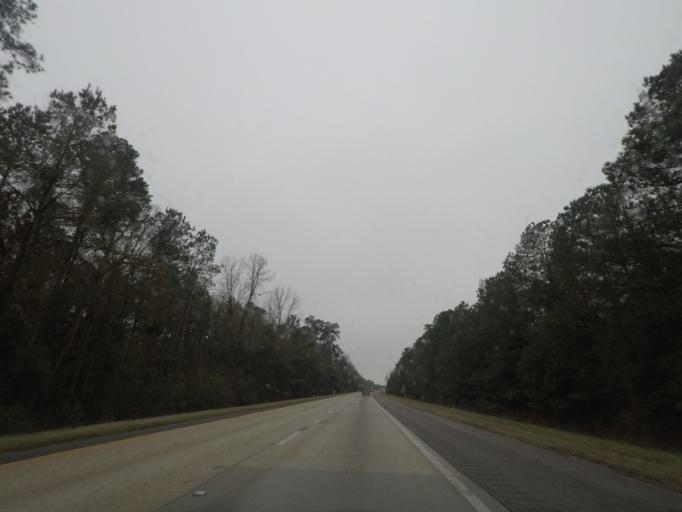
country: US
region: South Carolina
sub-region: Clarendon County
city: Manning
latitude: 33.7229
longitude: -80.2267
